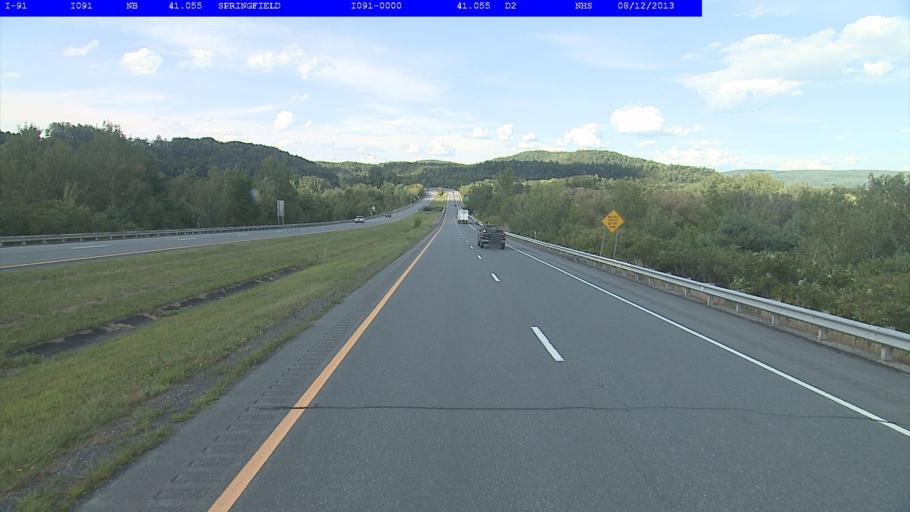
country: US
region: New Hampshire
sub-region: Sullivan County
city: Charlestown
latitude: 43.2585
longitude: -72.4376
